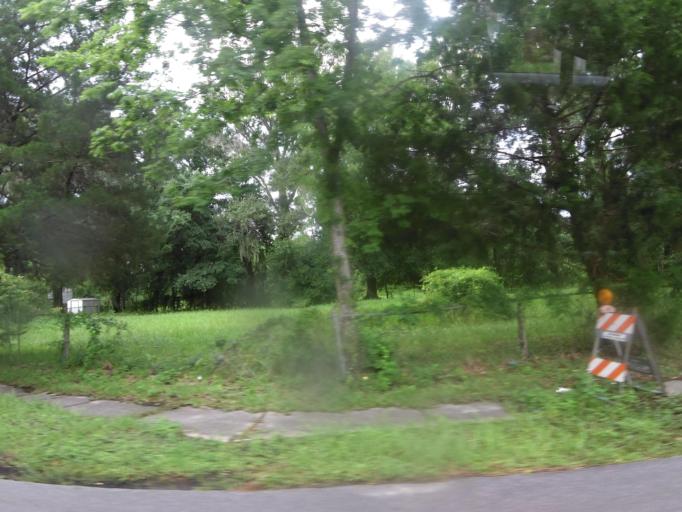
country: US
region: Florida
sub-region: Duval County
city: Jacksonville
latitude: 30.3058
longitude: -81.5519
